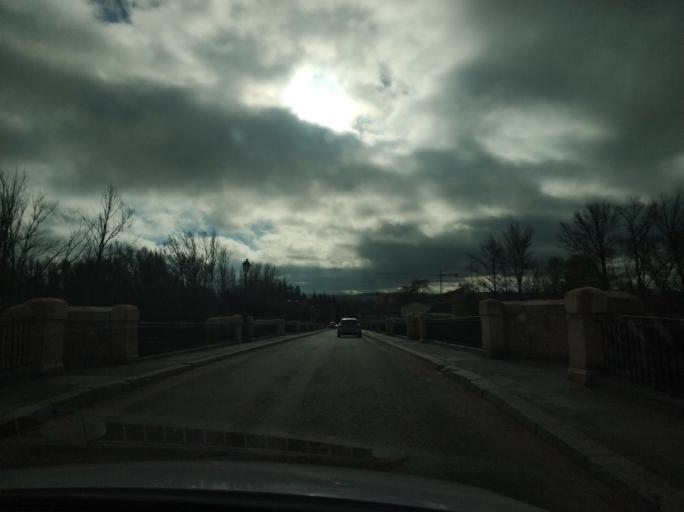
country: ES
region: Castille and Leon
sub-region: Provincia de Soria
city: San Esteban de Gormaz
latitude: 41.5727
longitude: -3.2055
